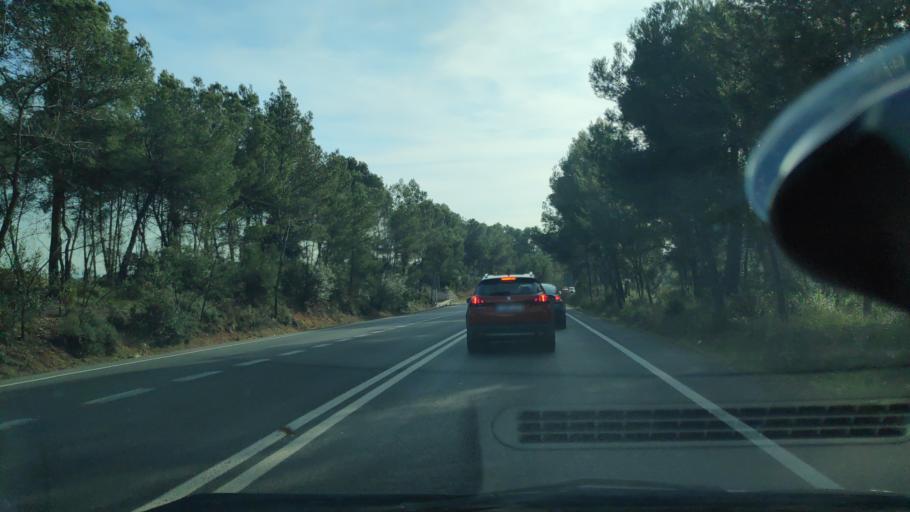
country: ES
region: Catalonia
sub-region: Provincia de Barcelona
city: Castellar del Valles
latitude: 41.5861
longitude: 2.0901
